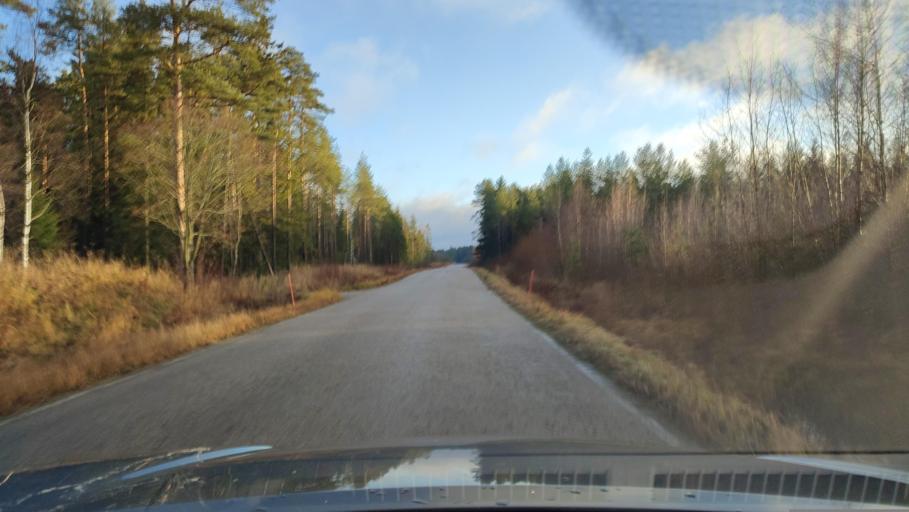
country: FI
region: Ostrobothnia
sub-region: Sydosterbotten
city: Naerpes
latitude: 62.4427
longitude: 21.3927
